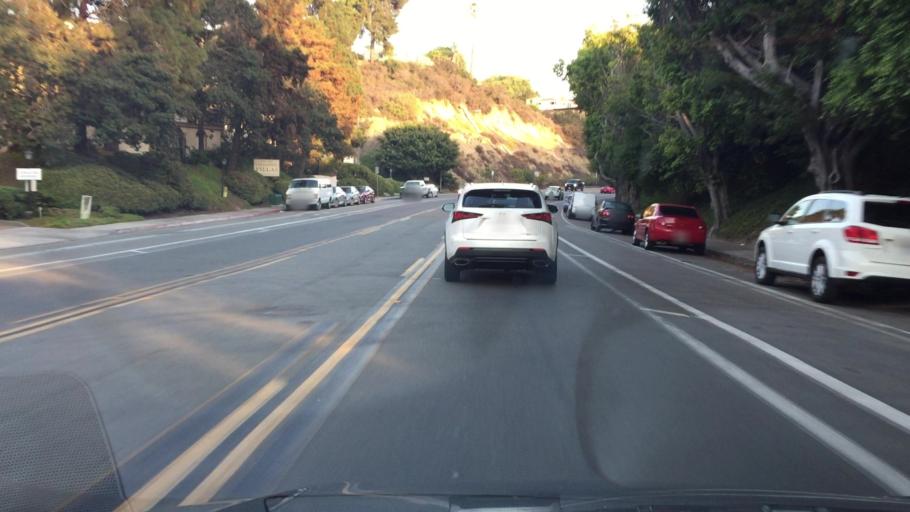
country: US
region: California
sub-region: San Diego County
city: Lemon Grove
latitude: 32.7677
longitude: -117.0846
